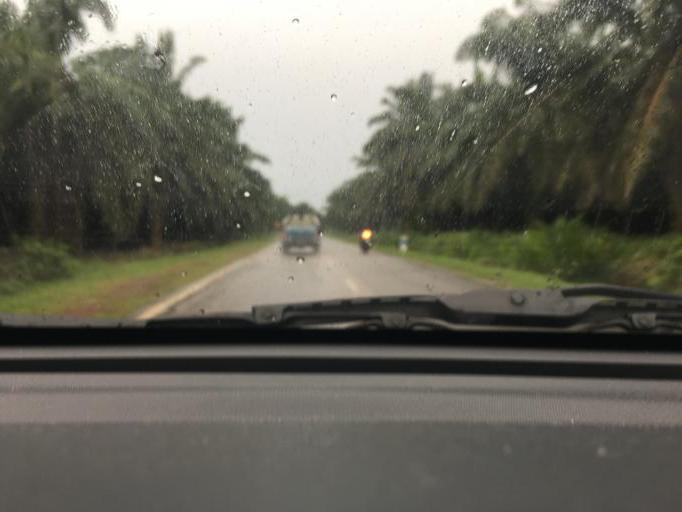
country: MY
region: Kedah
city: Bedong
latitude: 5.6525
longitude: 100.6335
